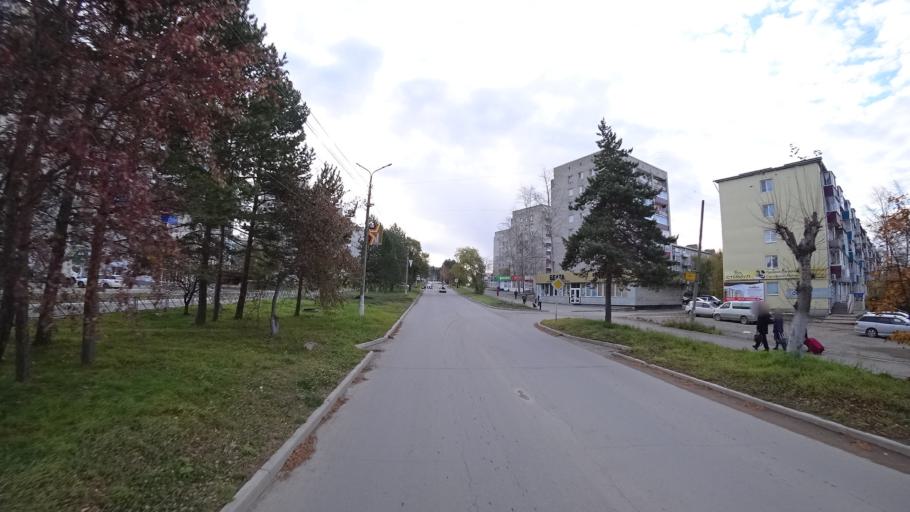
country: RU
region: Khabarovsk Krai
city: Amursk
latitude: 50.2285
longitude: 136.9059
